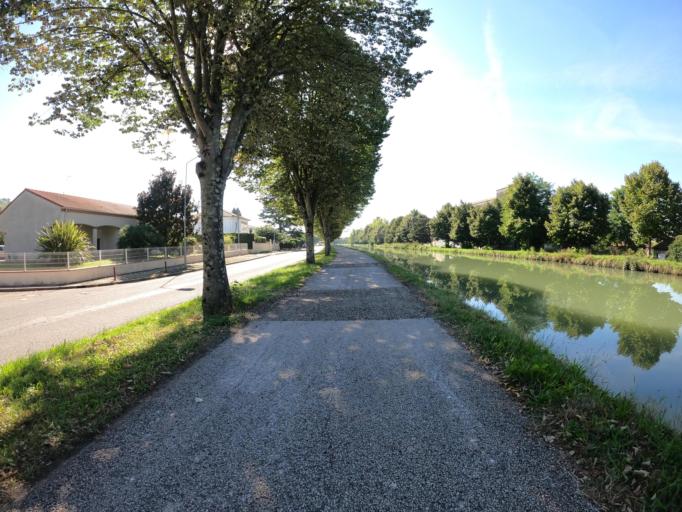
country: FR
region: Aquitaine
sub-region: Departement du Lot-et-Garonne
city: Agen
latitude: 44.2012
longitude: 0.6432
